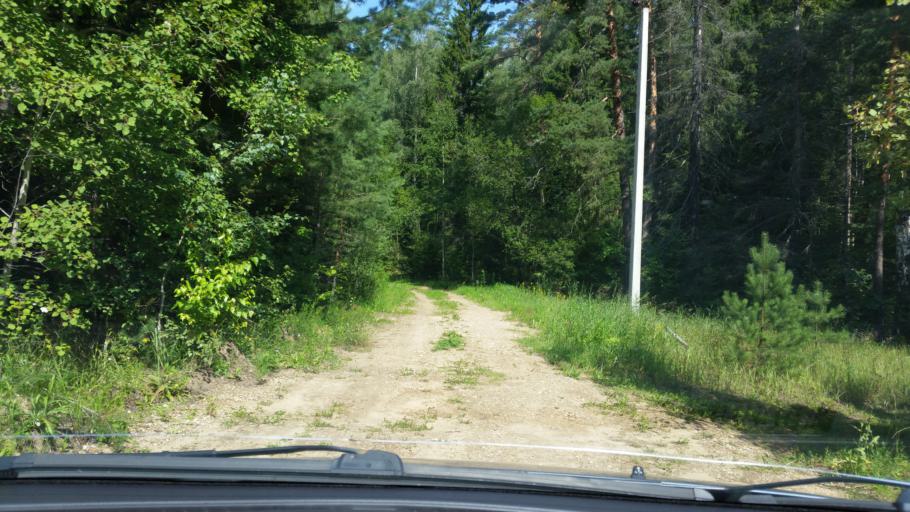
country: RU
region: Moskovskaya
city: Bol'shoye Gryzlovo
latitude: 54.9039
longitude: 37.7642
